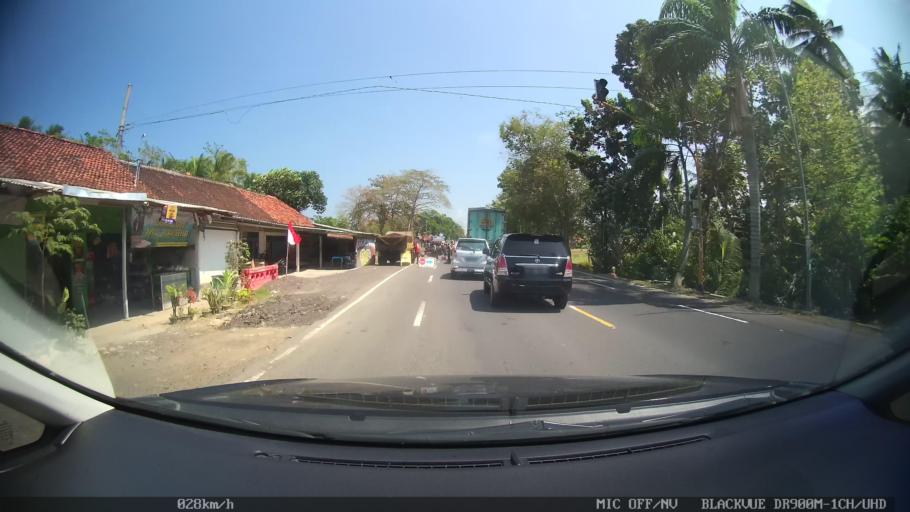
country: ID
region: Daerah Istimewa Yogyakarta
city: Srandakan
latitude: -7.8840
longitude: 110.0483
